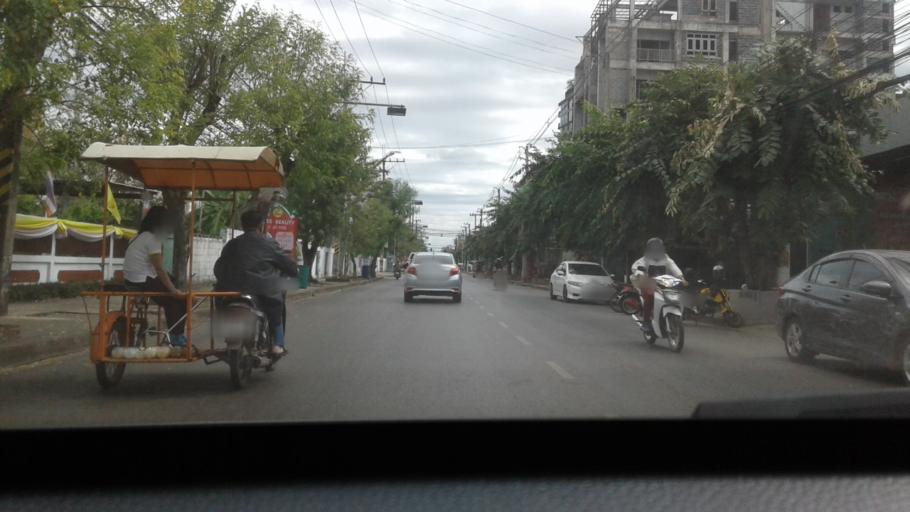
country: TH
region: Changwat Udon Thani
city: Udon Thani
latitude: 17.4125
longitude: 102.7939
